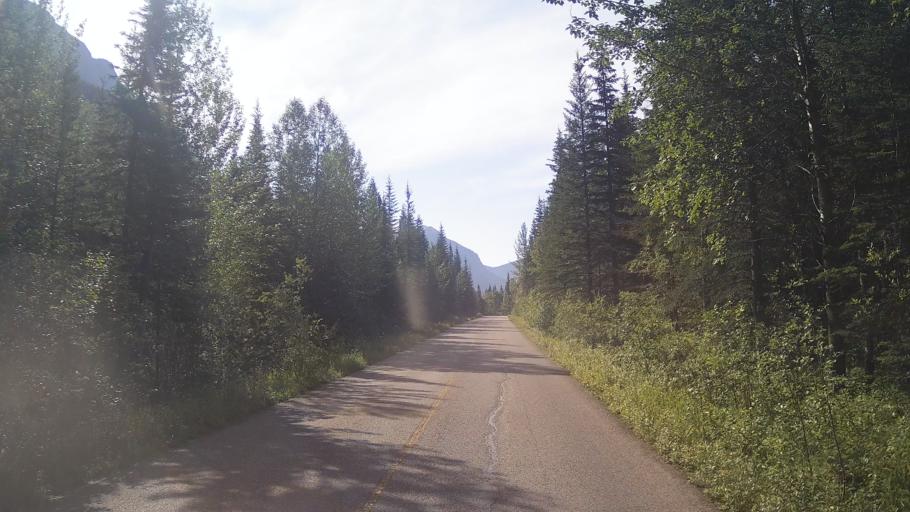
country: CA
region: Alberta
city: Hinton
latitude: 53.1757
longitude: -117.8306
